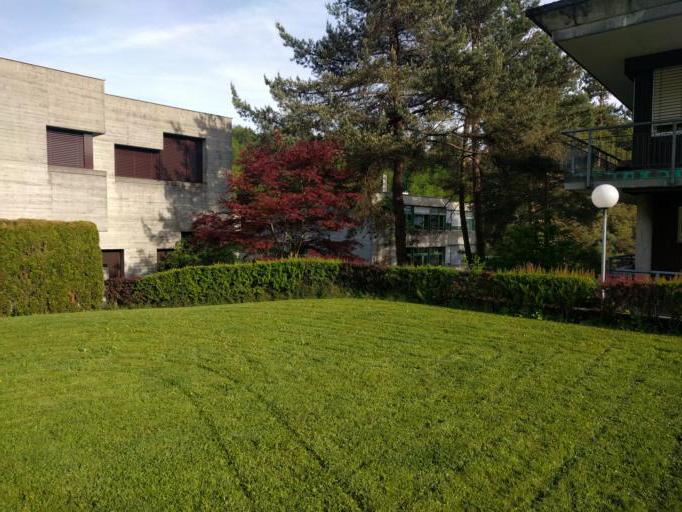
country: CH
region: Lucerne
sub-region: Lucerne-Land District
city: Adligenswil
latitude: 47.0556
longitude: 8.3442
